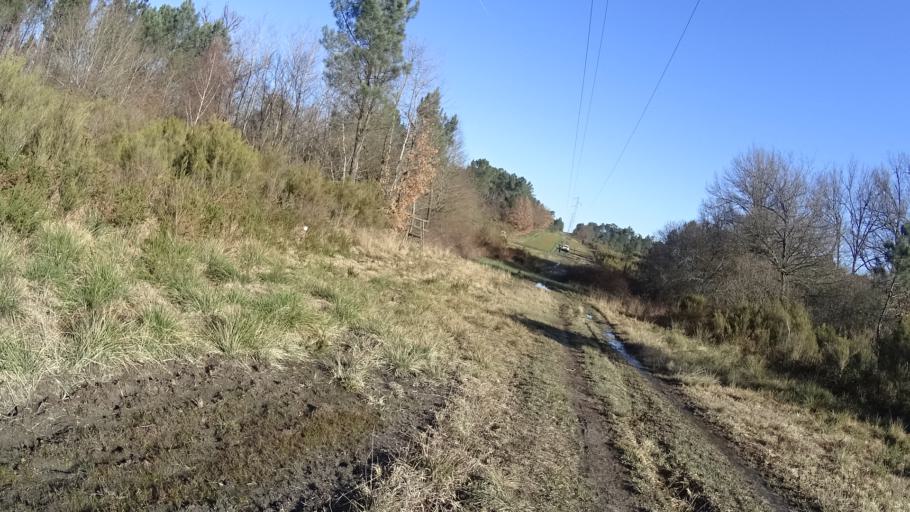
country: FR
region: Aquitaine
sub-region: Departement de la Dordogne
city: La Roche-Chalais
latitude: 45.1635
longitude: 0.0315
